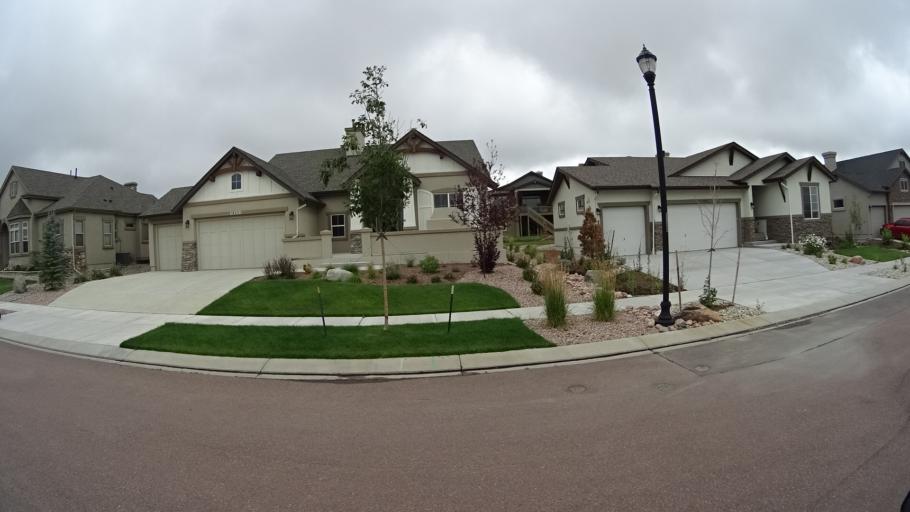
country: US
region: Colorado
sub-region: El Paso County
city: Gleneagle
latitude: 39.0118
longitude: -104.7910
